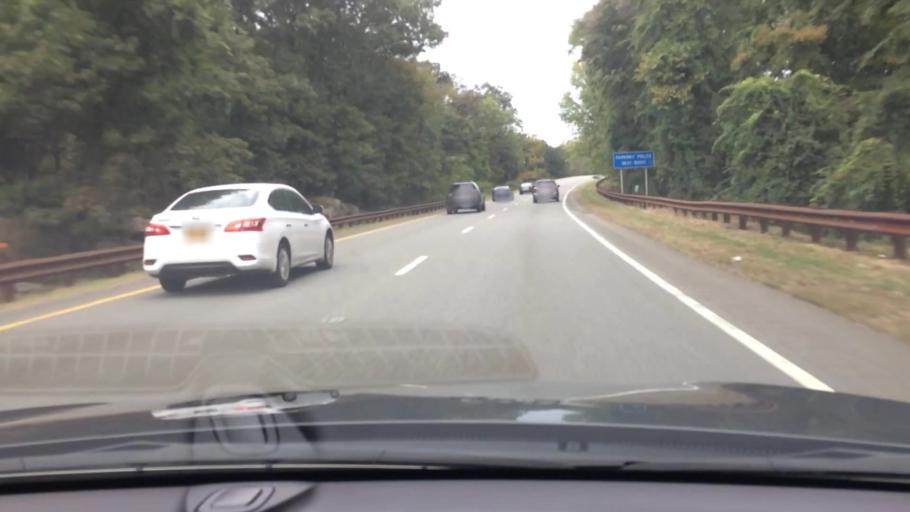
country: US
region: New Jersey
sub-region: Bergen County
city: Alpine
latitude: 40.9525
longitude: -73.9214
